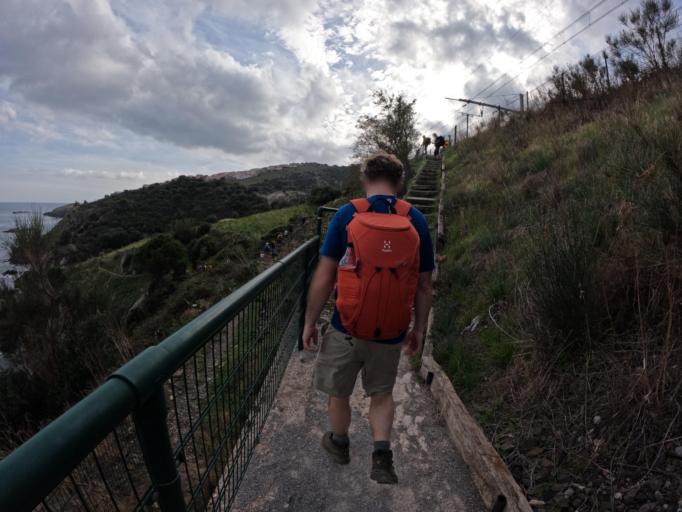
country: FR
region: Languedoc-Roussillon
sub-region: Departement des Pyrenees-Orientales
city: Cervera de la Marenda
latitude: 42.4521
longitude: 3.1591
